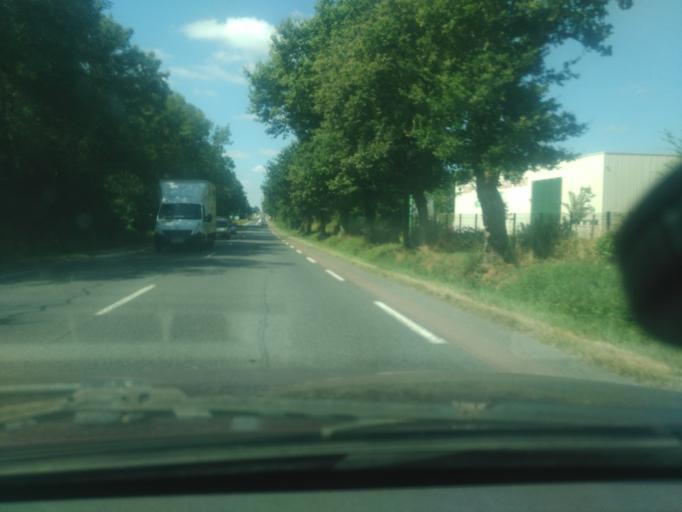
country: FR
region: Pays de la Loire
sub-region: Departement de la Vendee
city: Les Essarts
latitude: 46.7635
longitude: -1.2402
